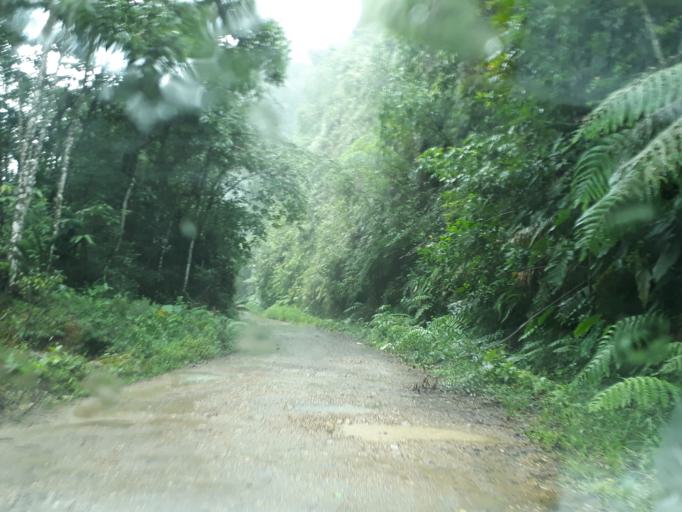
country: CO
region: Boyaca
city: Santa Maria
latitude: 4.7281
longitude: -73.3029
